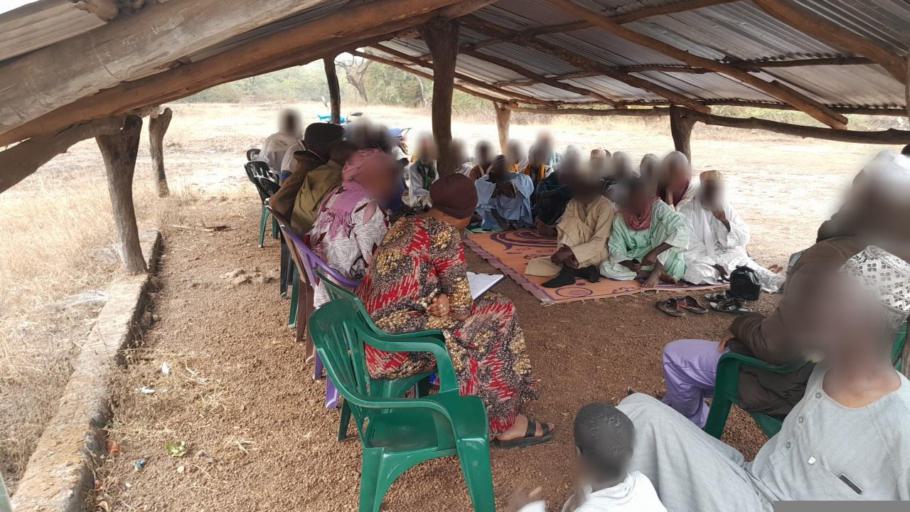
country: GN
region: Mamou
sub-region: Dalaba
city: Dalaba
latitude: 10.7964
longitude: -12.0915
